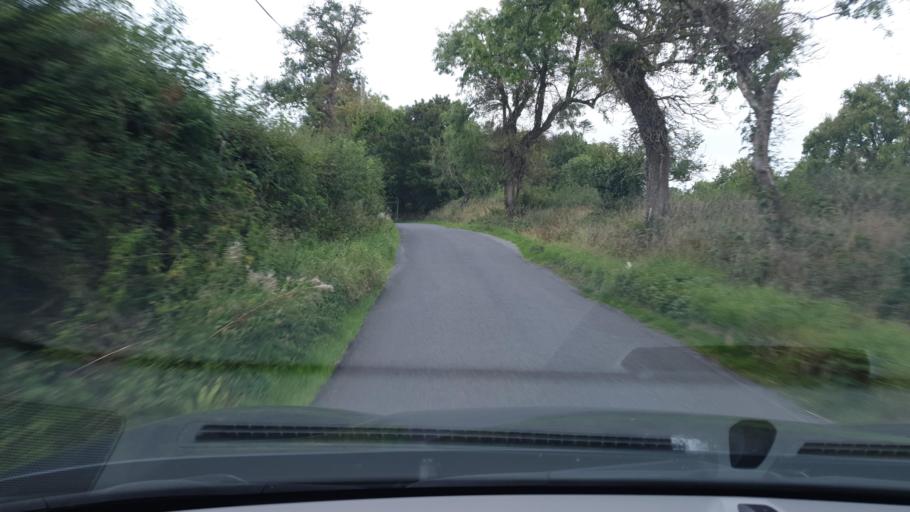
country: IE
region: Leinster
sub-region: An Mhi
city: Ratoath
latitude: 53.5243
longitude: -6.4850
